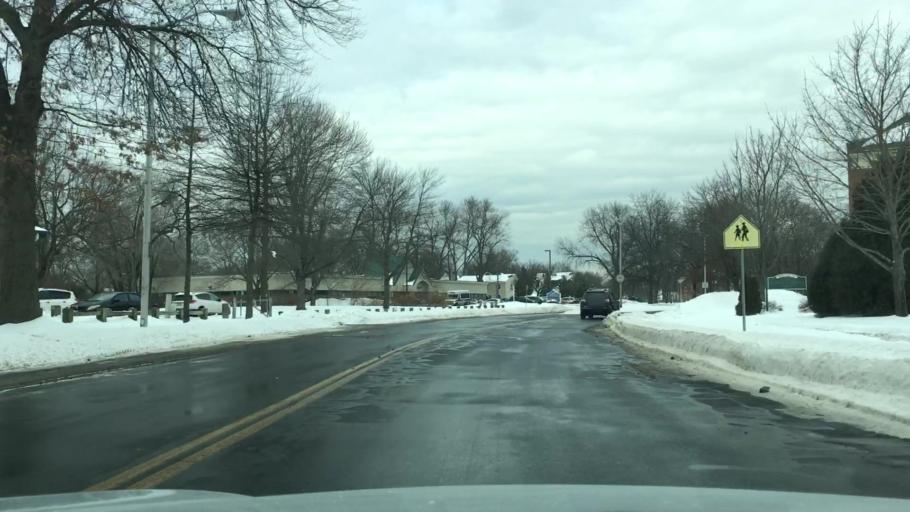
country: US
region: Massachusetts
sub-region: Hampden County
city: West Springfield
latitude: 42.1163
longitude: -72.6131
